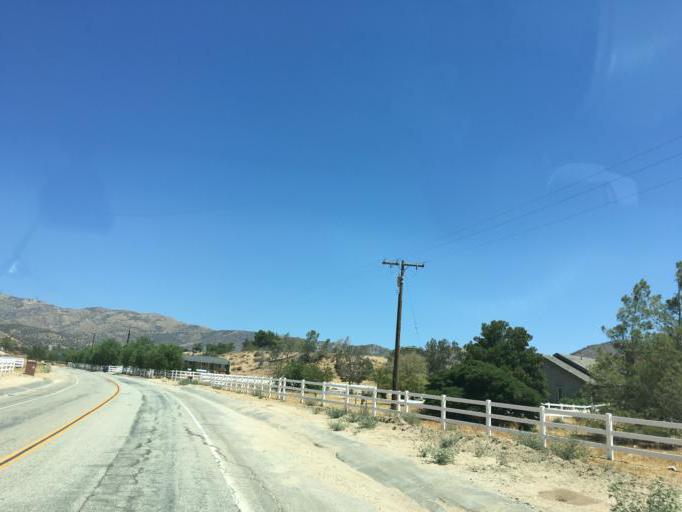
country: US
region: California
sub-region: Los Angeles County
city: Acton
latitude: 34.5081
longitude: -118.2162
